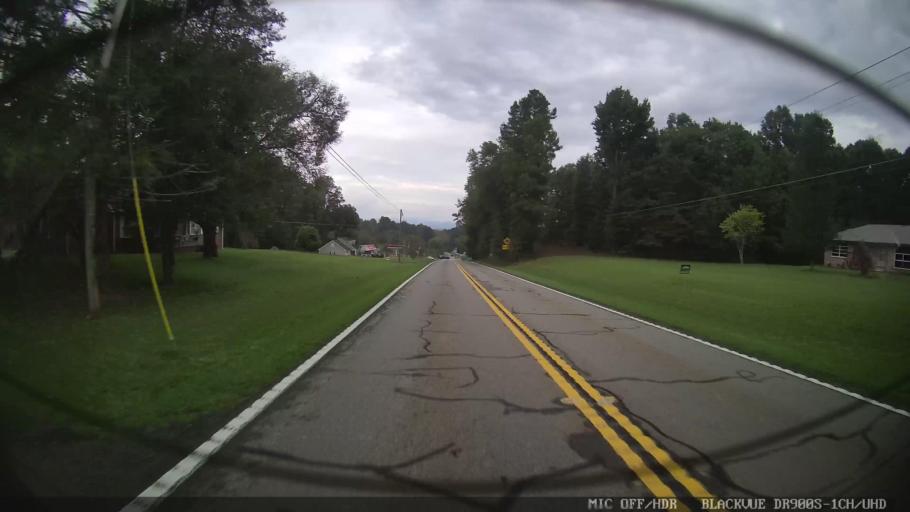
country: US
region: Georgia
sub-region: Gilmer County
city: Ellijay
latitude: 34.7291
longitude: -84.5099
